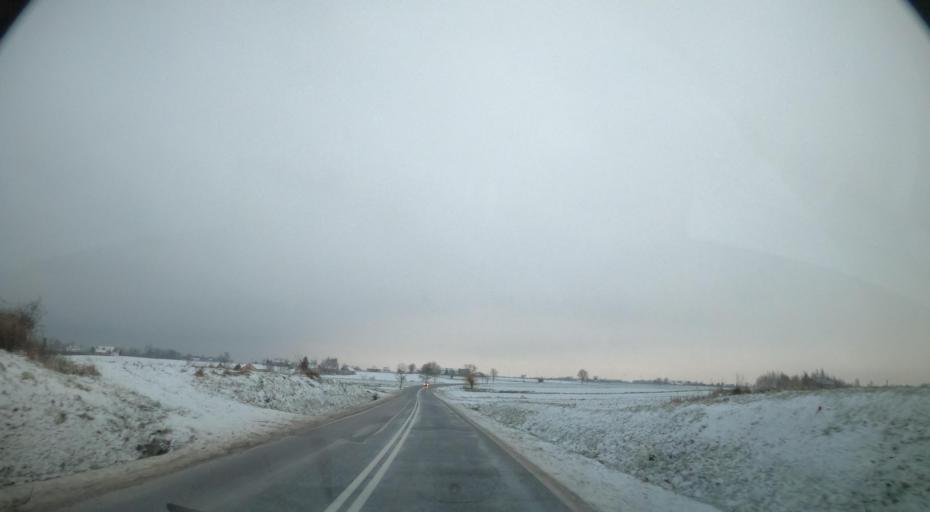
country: PL
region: Kujawsko-Pomorskie
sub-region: Powiat lipnowski
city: Dobrzyn nad Wisla
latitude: 52.6362
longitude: 19.4051
